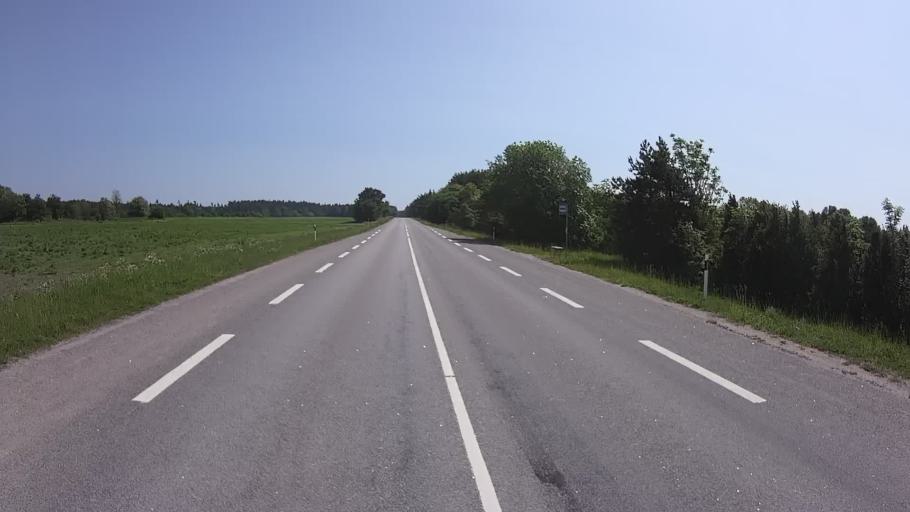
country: EE
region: Saare
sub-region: Kuressaare linn
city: Kuressaare
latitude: 58.3636
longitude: 22.0569
